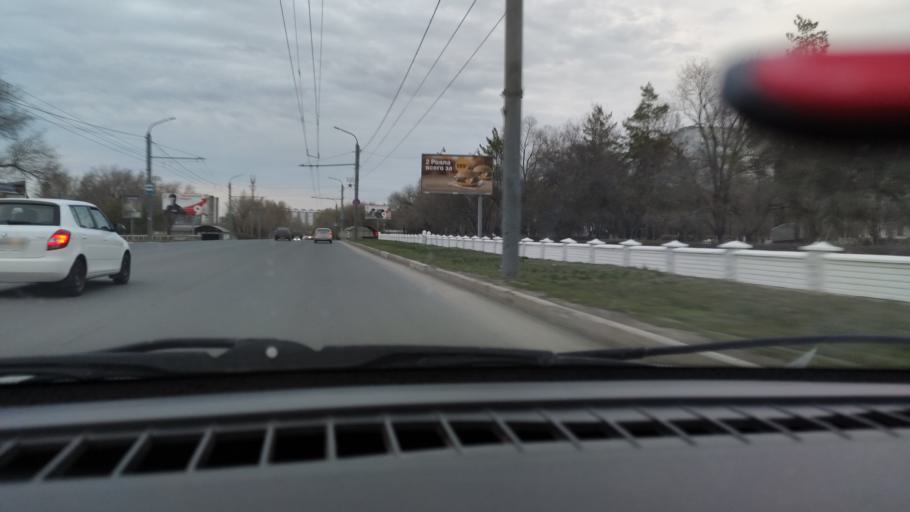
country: RU
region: Orenburg
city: Orenburg
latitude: 51.8025
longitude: 55.1375
